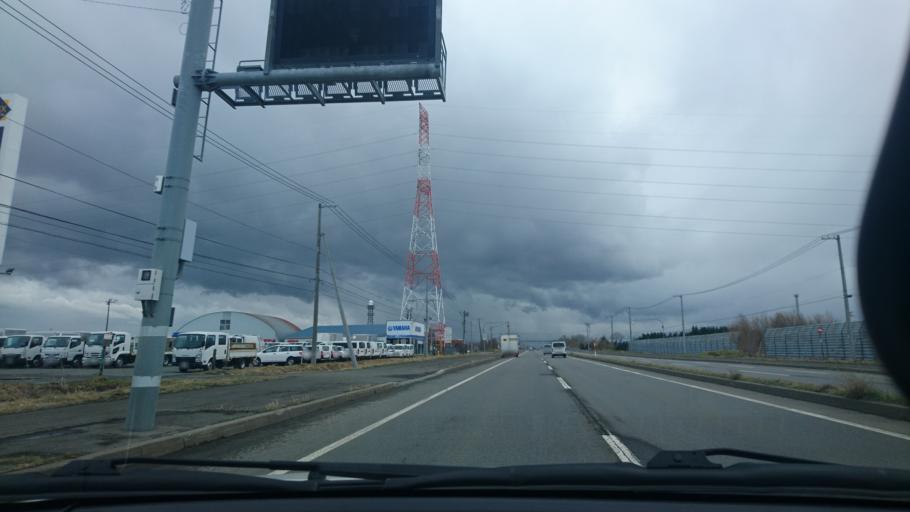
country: JP
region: Hokkaido
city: Ishikari
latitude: 43.2054
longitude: 141.3321
